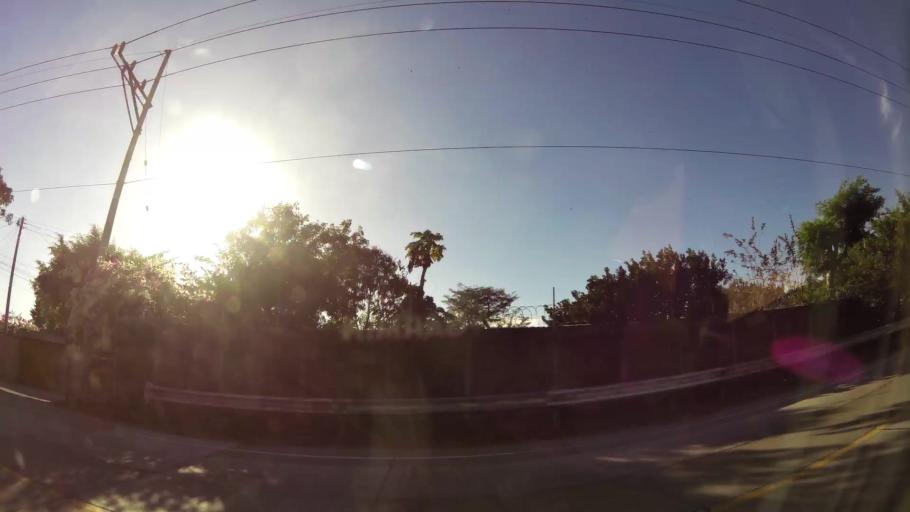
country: SV
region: Santa Ana
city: Metapan
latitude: 14.2415
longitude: -89.4727
